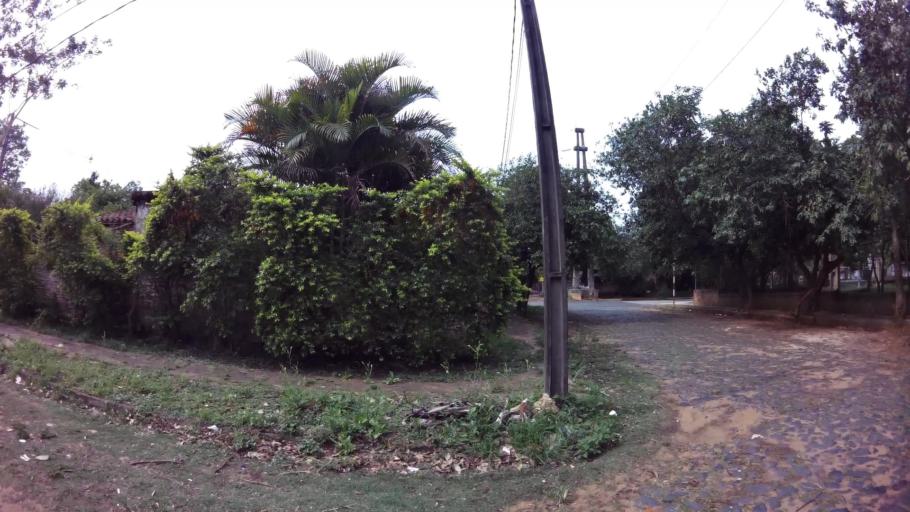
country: PY
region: Central
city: Fernando de la Mora
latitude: -25.2949
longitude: -57.5687
